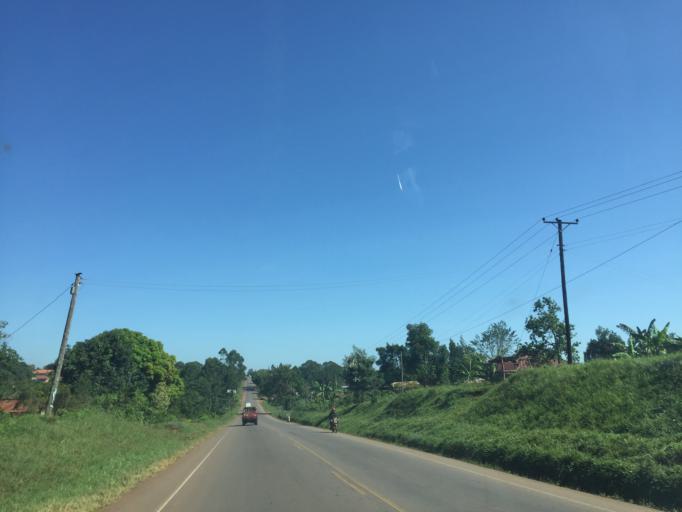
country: UG
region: Central Region
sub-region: Luwero District
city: Wobulenzi
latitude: 0.7421
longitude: 32.5168
